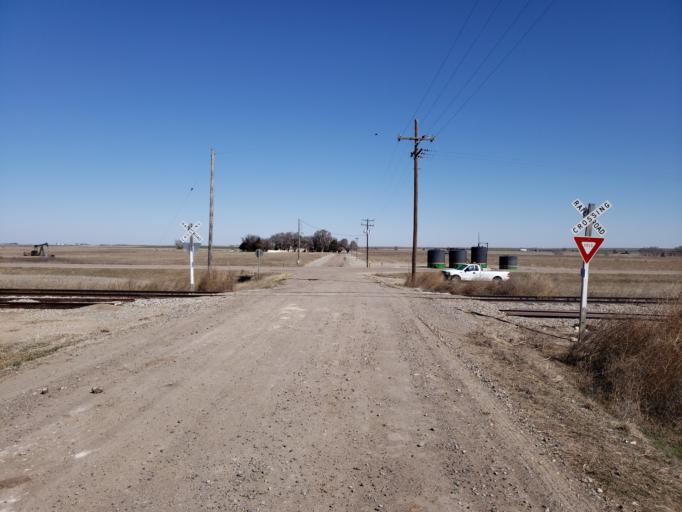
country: US
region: Kansas
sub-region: Ness County
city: Ness City
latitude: 38.4514
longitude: -99.9353
